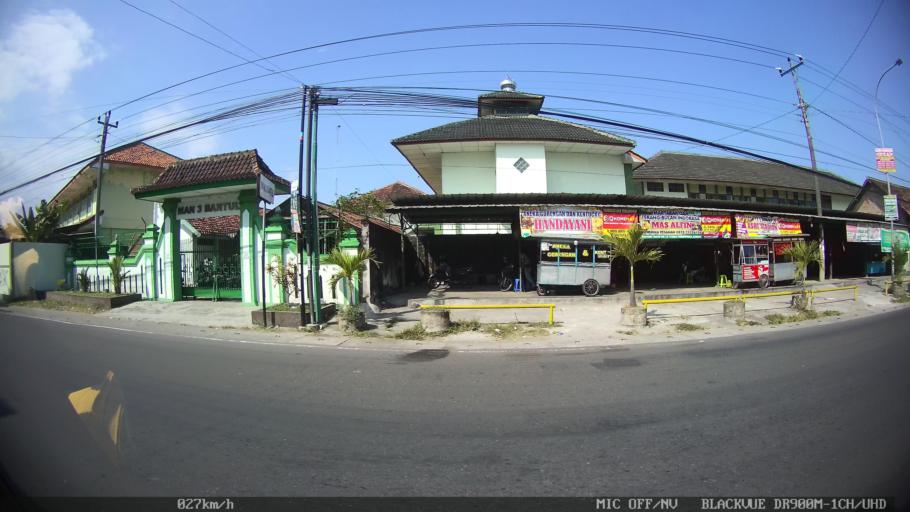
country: ID
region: Daerah Istimewa Yogyakarta
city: Sewon
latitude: -7.8695
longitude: 110.3909
